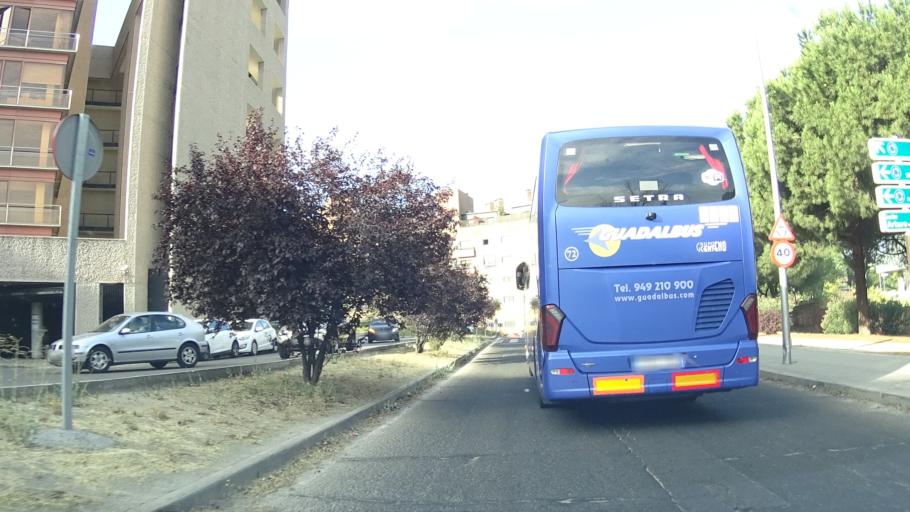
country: ES
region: Madrid
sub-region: Provincia de Madrid
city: Ciudad Lineal
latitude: 40.4479
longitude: -3.6368
